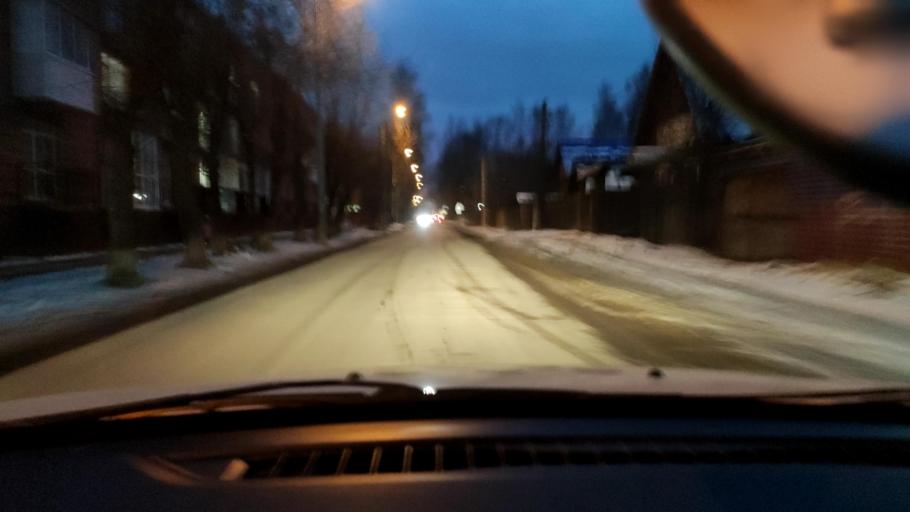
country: RU
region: Perm
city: Overyata
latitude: 58.0107
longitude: 55.9553
